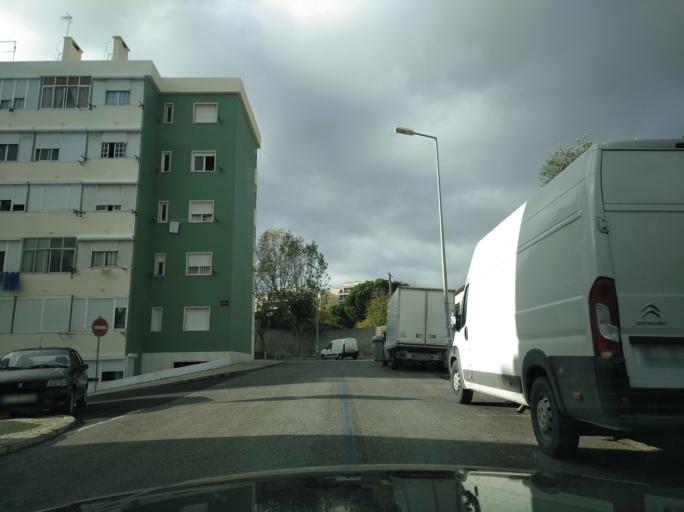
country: PT
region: Lisbon
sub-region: Loures
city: Sacavem
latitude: 38.7959
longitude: -9.1092
